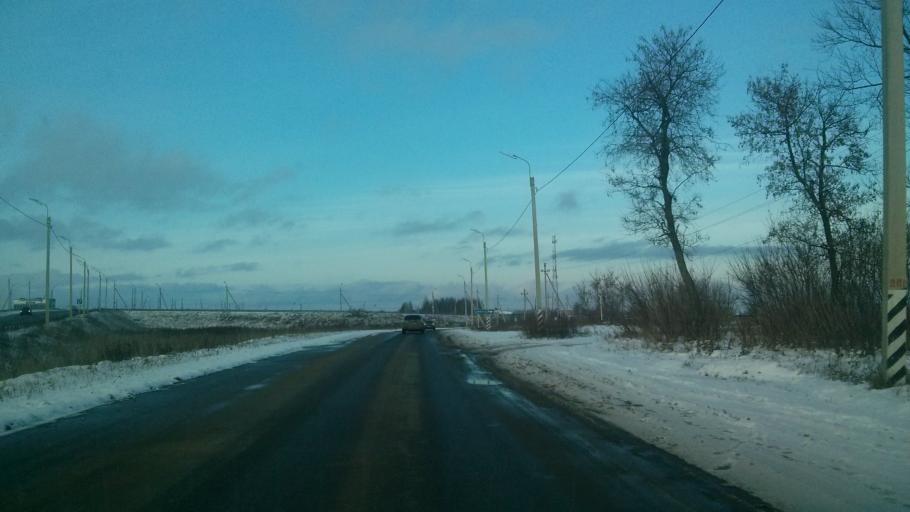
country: RU
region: Vladimir
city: Murom
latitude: 55.6149
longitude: 42.0262
